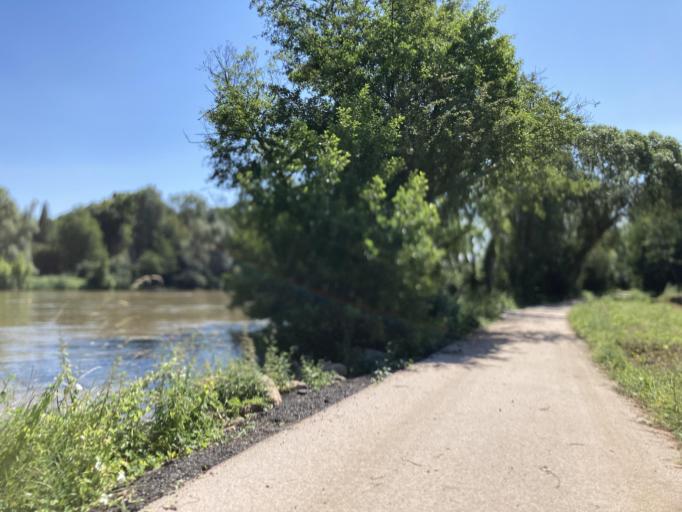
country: FR
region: Bourgogne
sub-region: Departement de l'Yonne
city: Laroche-Saint-Cydroine
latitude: 47.9646
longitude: 3.4575
